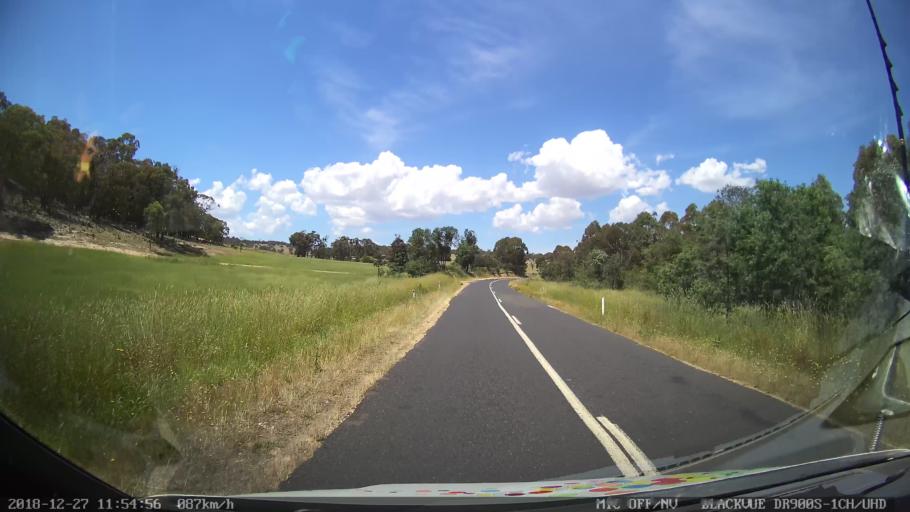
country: AU
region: New South Wales
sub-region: Blayney
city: Blayney
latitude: -33.6814
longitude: 149.4011
